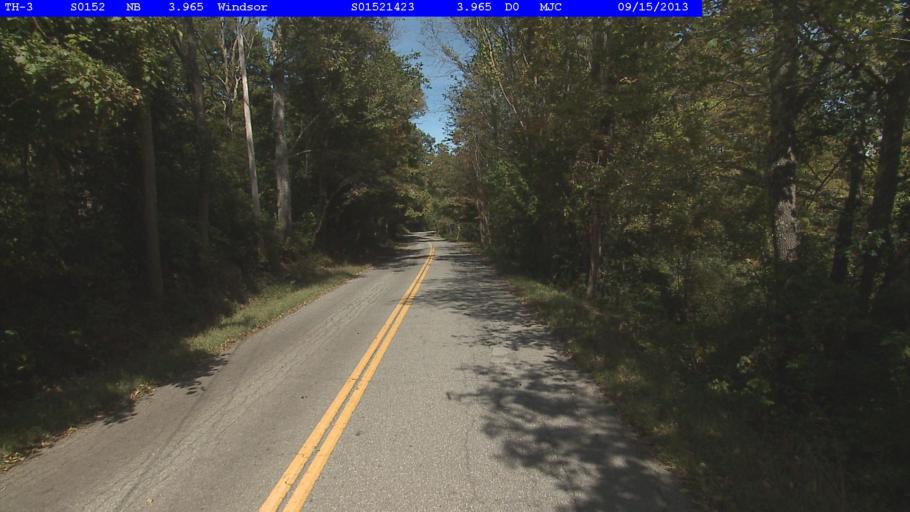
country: US
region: Vermont
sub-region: Windsor County
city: Windsor
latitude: 43.5177
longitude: -72.4331
